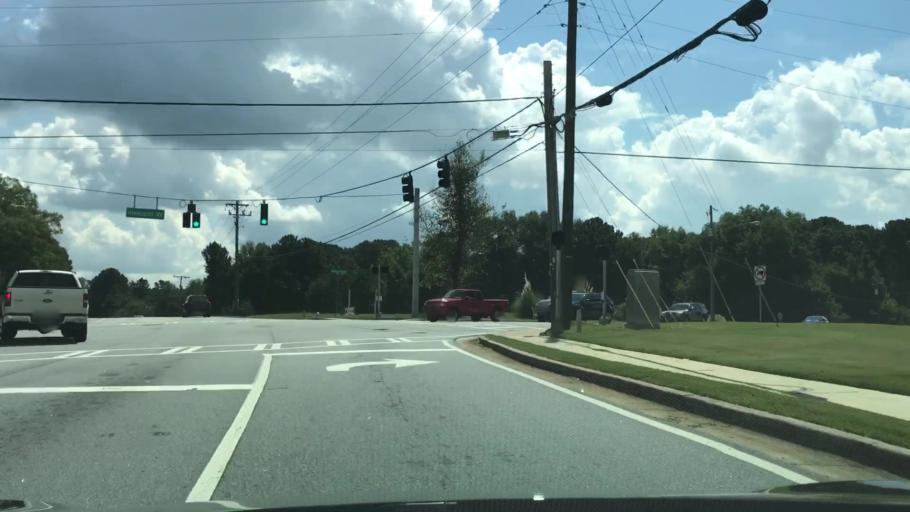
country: US
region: Georgia
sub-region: Gwinnett County
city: Snellville
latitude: 33.8726
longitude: -84.0504
